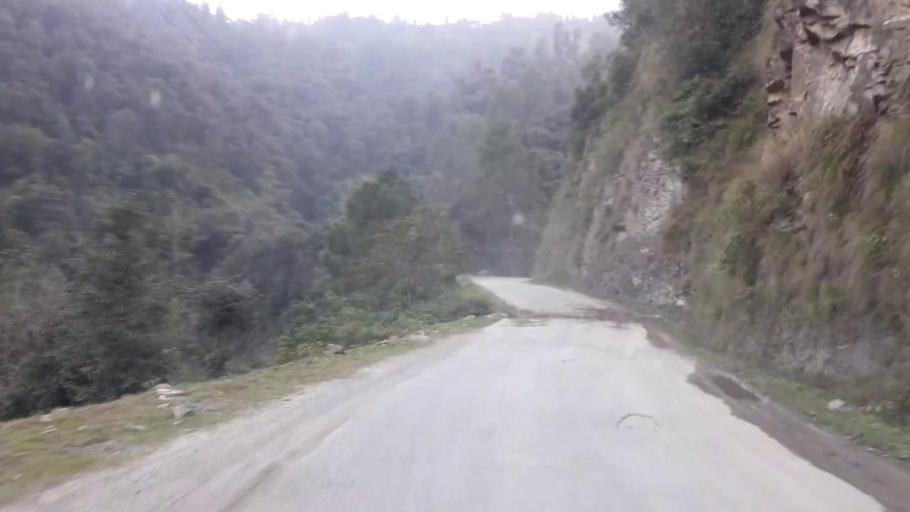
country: IN
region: Himachal Pradesh
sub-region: Shimla
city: Shimla
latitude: 31.0584
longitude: 77.1505
